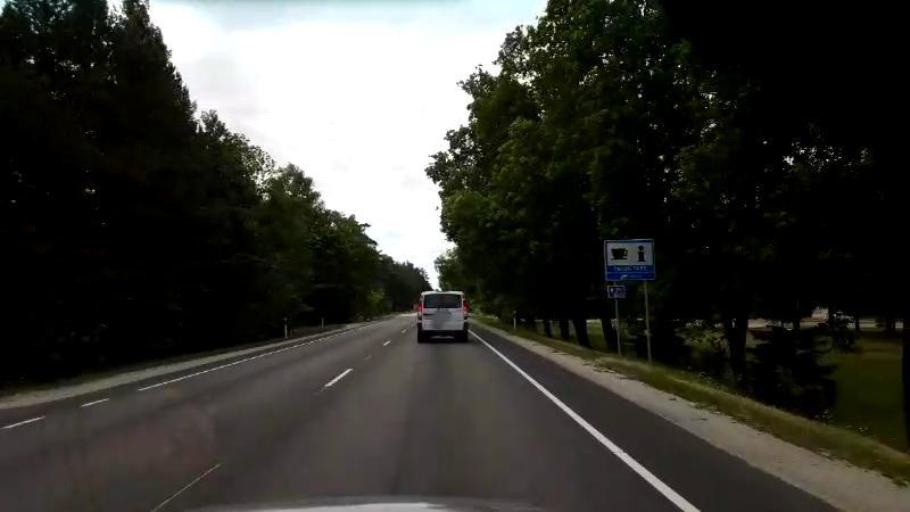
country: EE
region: Paernumaa
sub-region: Paernu linn
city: Parnu
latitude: 58.2185
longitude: 24.4883
